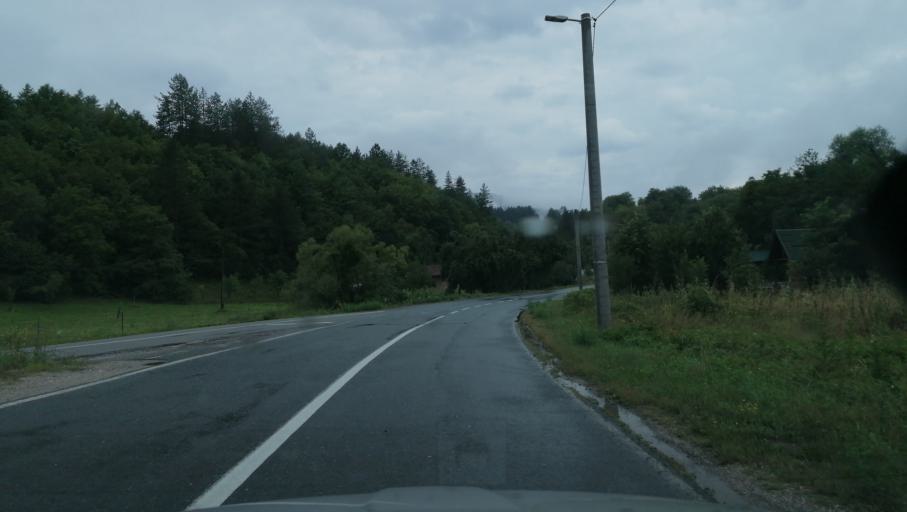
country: RS
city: Durici
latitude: 43.7488
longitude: 19.4018
